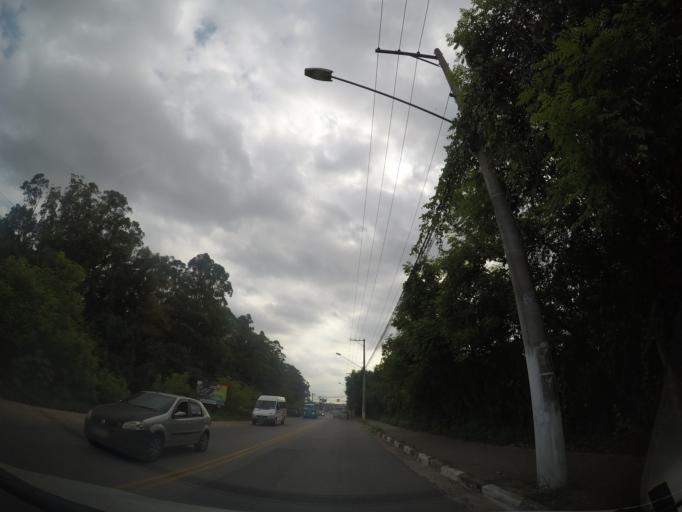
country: BR
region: Sao Paulo
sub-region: Guarulhos
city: Guarulhos
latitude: -23.4214
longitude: -46.4893
